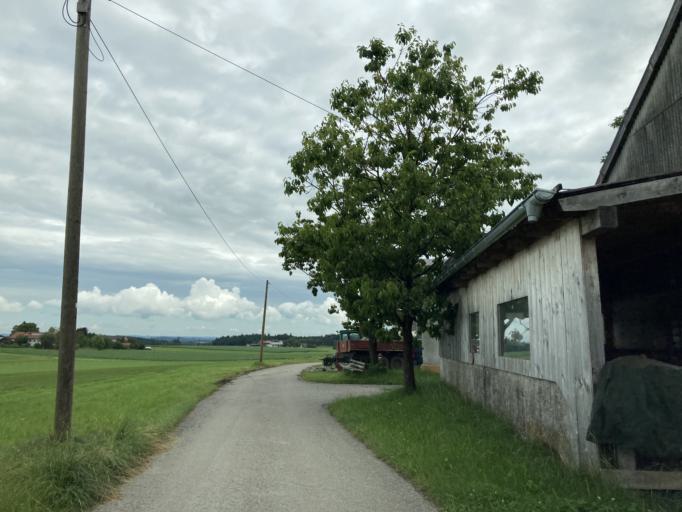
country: DE
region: Bavaria
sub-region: Upper Bavaria
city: Vogtareuth
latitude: 47.9209
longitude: 12.1933
